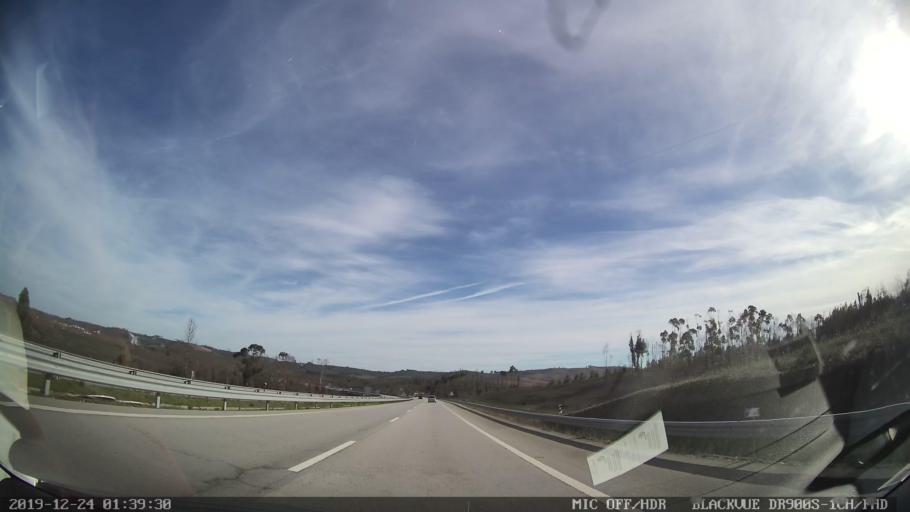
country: PT
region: Portalegre
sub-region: Gaviao
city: Gaviao
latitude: 39.5333
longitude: -7.9073
